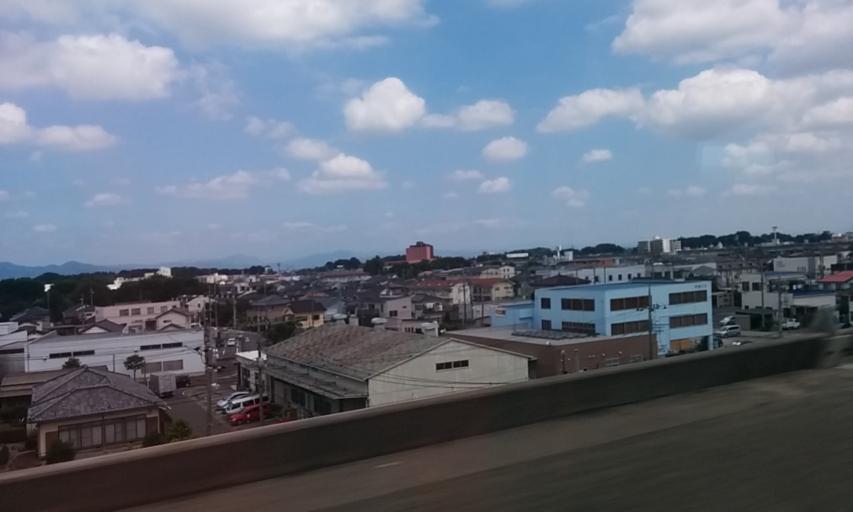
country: JP
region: Tochigi
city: Oyama
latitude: 36.2979
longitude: 139.7953
